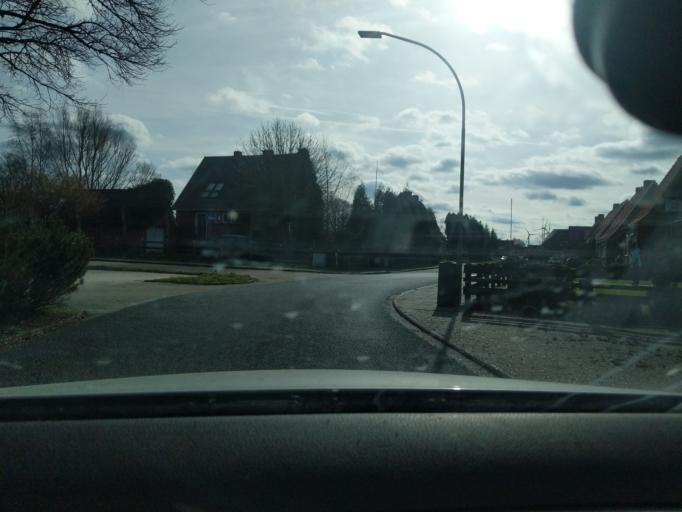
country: DE
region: Lower Saxony
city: Drochtersen
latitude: 53.7135
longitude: 9.3850
